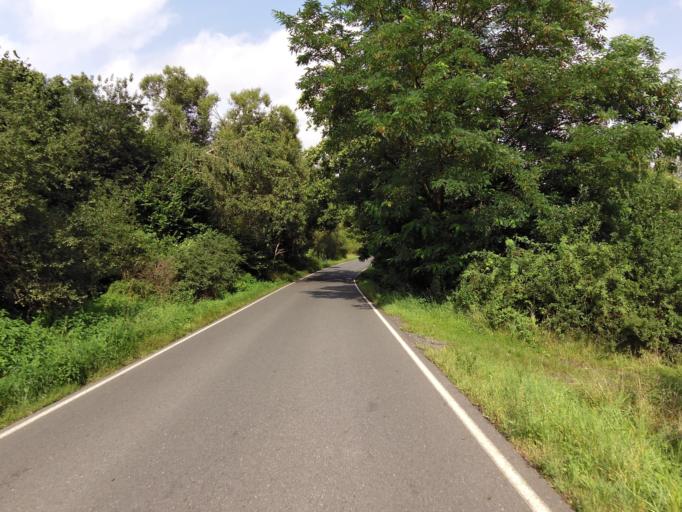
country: CZ
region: Central Bohemia
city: Tynec nad Sazavou
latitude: 49.8666
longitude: 14.5852
